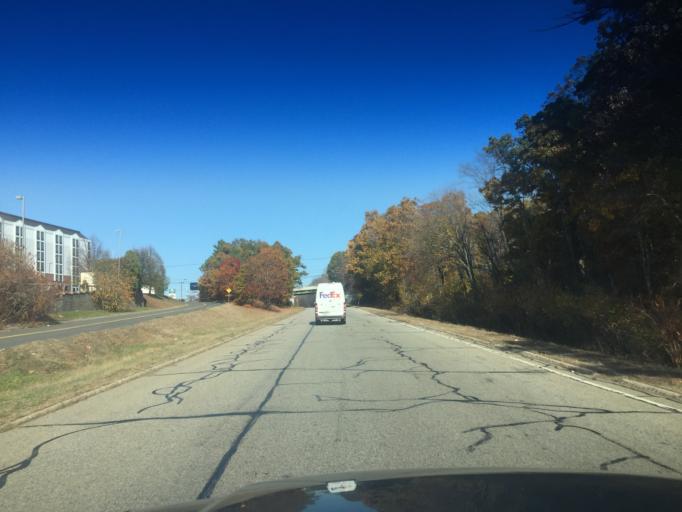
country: US
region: Massachusetts
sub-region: Essex County
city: South Peabody
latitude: 42.5249
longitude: -70.9934
